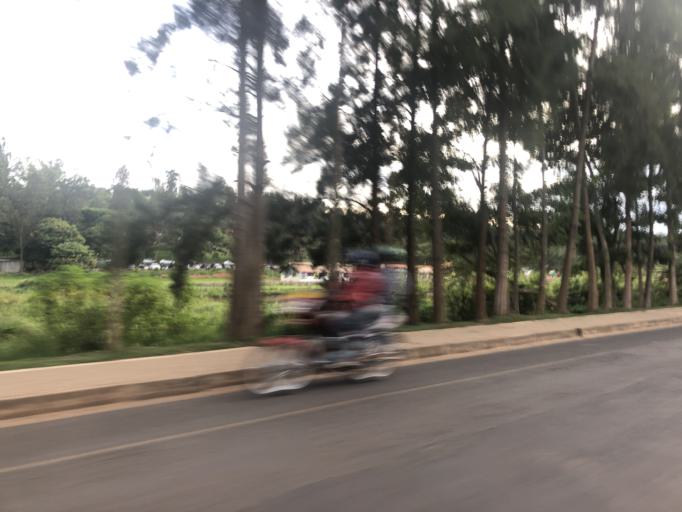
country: RW
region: Kigali
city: Kigali
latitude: -1.9306
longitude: 30.0820
